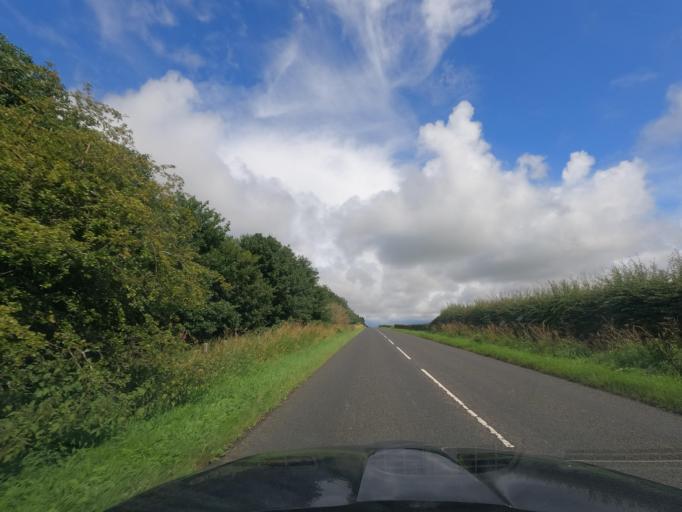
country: GB
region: England
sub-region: Northumberland
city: Lowick
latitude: 55.6104
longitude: -1.9997
